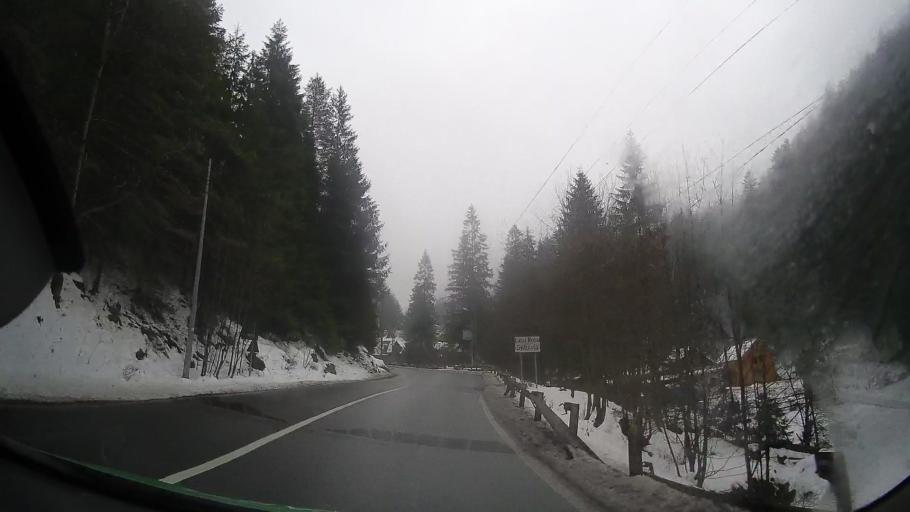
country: RO
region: Neamt
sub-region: Comuna Bicaz Chei
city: Bicaz Chei
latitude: 46.7990
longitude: 25.8013
